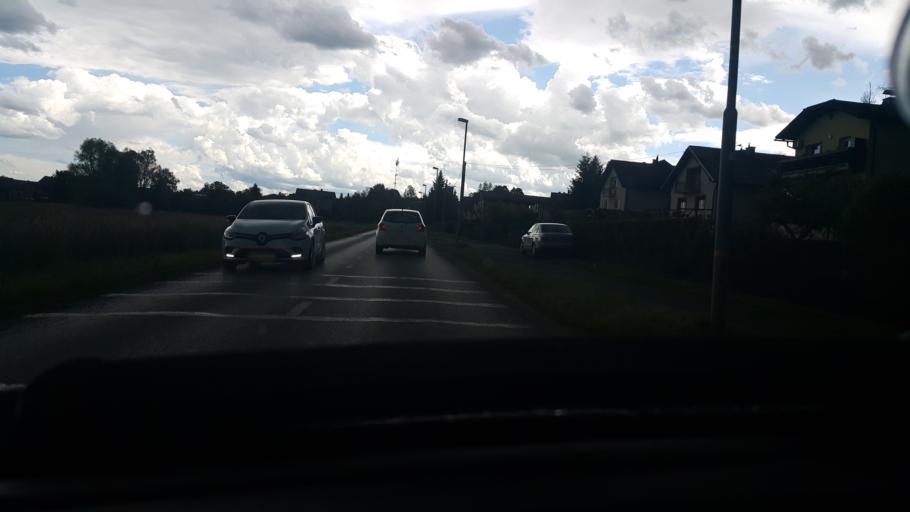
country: SI
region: Maribor
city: Razvanje
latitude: 46.5211
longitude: 15.6351
